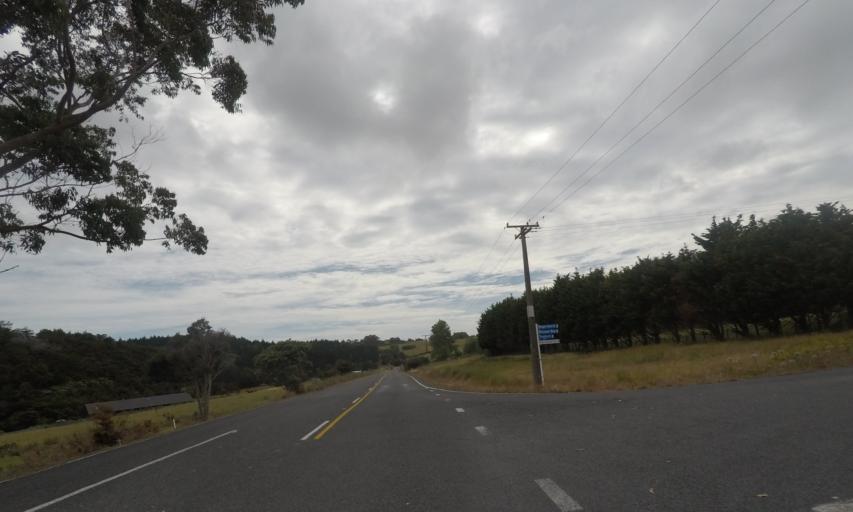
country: NZ
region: Northland
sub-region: Whangarei
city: Ruakaka
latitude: -35.7681
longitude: 174.4876
